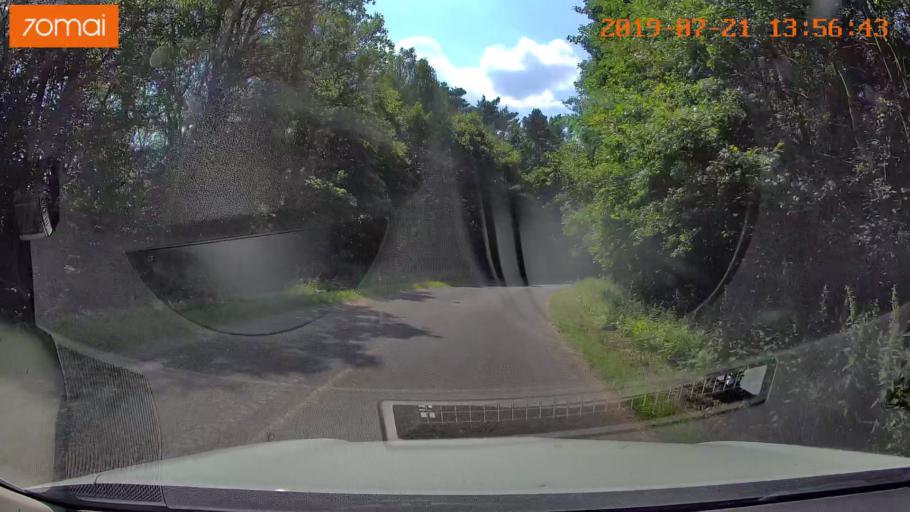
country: BY
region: Grodnenskaya
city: Lyubcha
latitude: 53.7768
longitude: 26.0978
